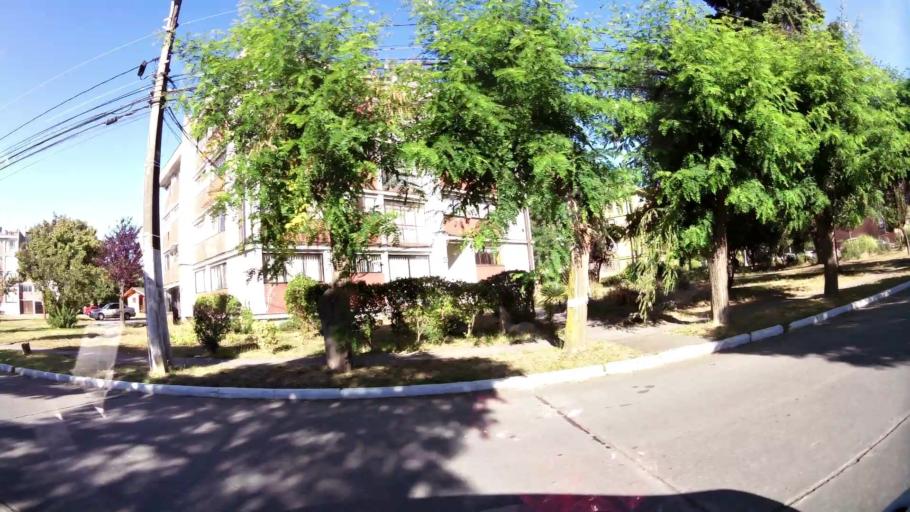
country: CL
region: Biobio
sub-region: Provincia de Concepcion
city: Concepcion
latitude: -36.8412
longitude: -73.1073
